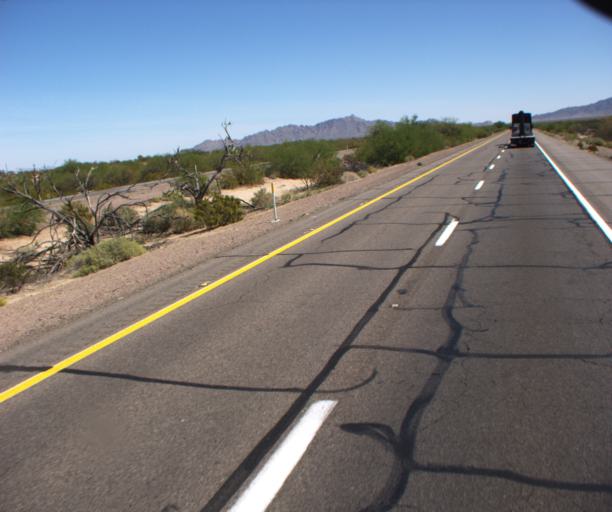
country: US
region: Arizona
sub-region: Yuma County
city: Wellton
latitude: 32.7045
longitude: -113.8800
